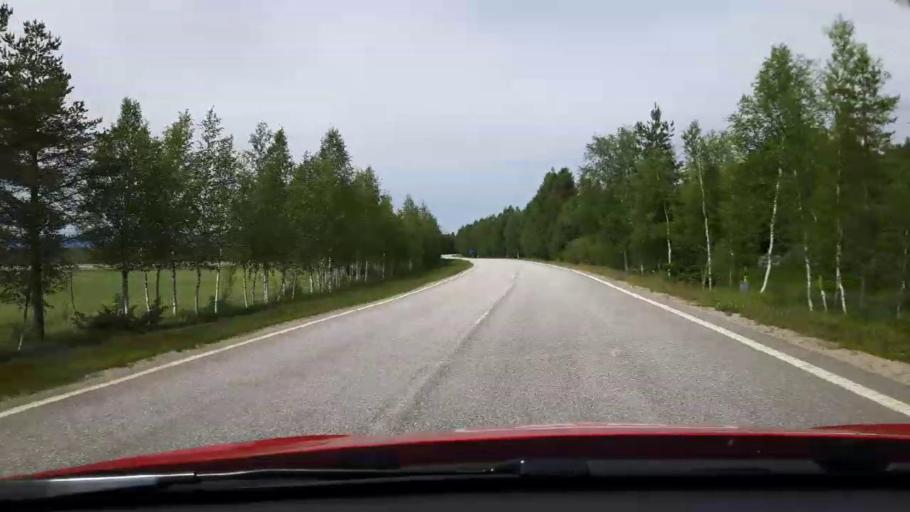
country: SE
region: Jaemtland
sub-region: Harjedalens Kommun
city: Sveg
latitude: 62.1279
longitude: 14.0659
